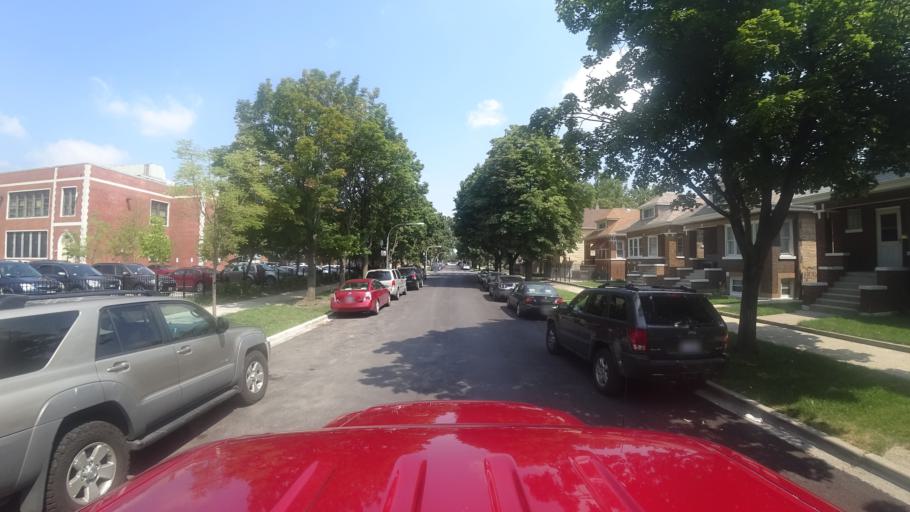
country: US
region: Illinois
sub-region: Cook County
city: Cicero
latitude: 41.8054
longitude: -87.7248
